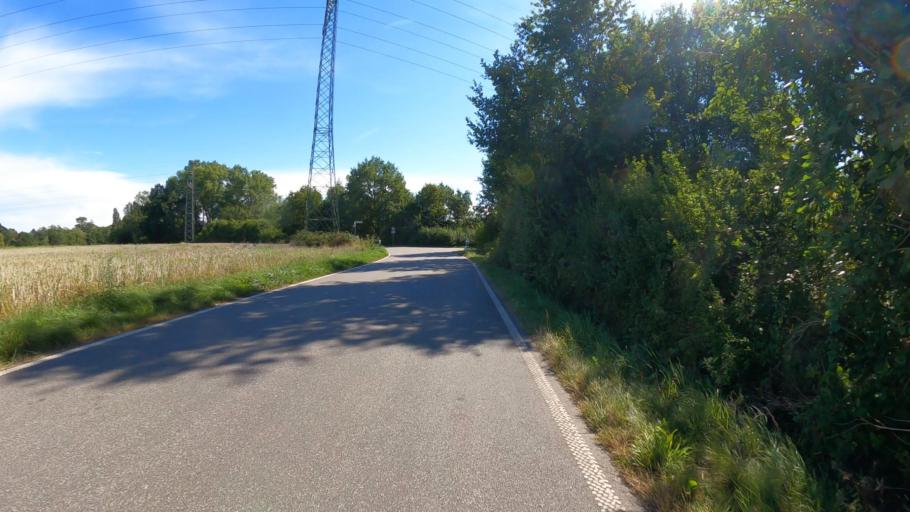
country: DE
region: Schleswig-Holstein
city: Gross Schenkenberg
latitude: 53.8079
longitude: 10.5816
